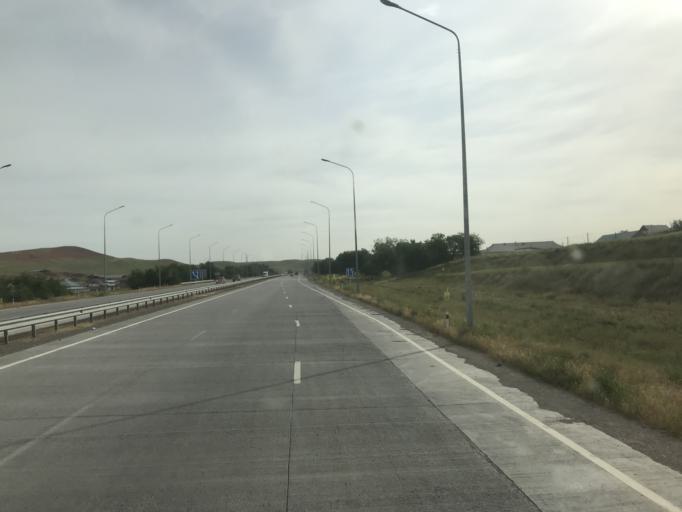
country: KZ
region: Ongtustik Qazaqstan
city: Shymkent
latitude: 42.2139
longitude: 69.5229
